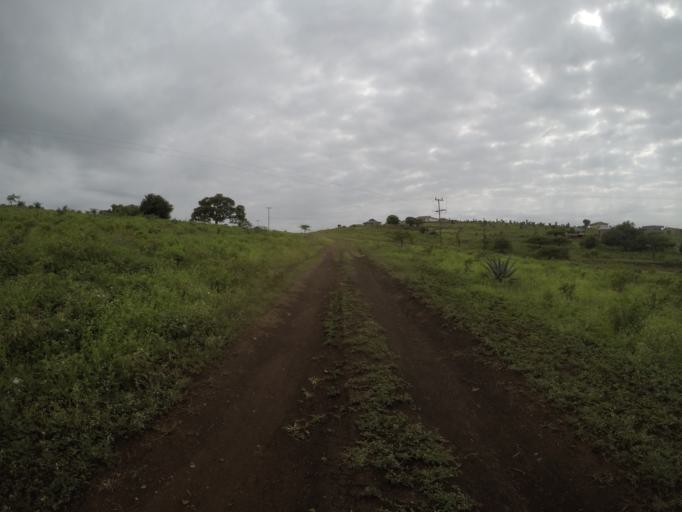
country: ZA
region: KwaZulu-Natal
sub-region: uThungulu District Municipality
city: Empangeni
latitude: -28.6379
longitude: 31.9042
